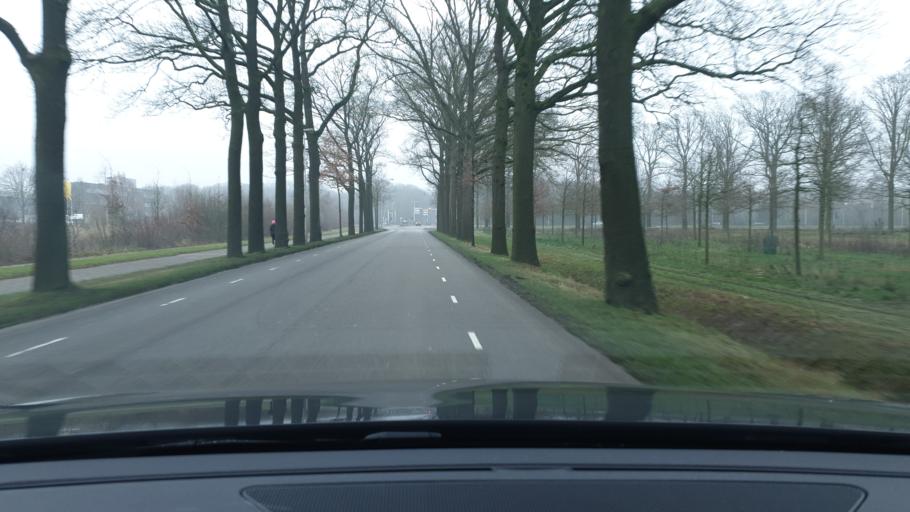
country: NL
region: North Brabant
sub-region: Gemeente Eindhoven
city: Meerhoven
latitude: 51.4652
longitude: 5.4144
